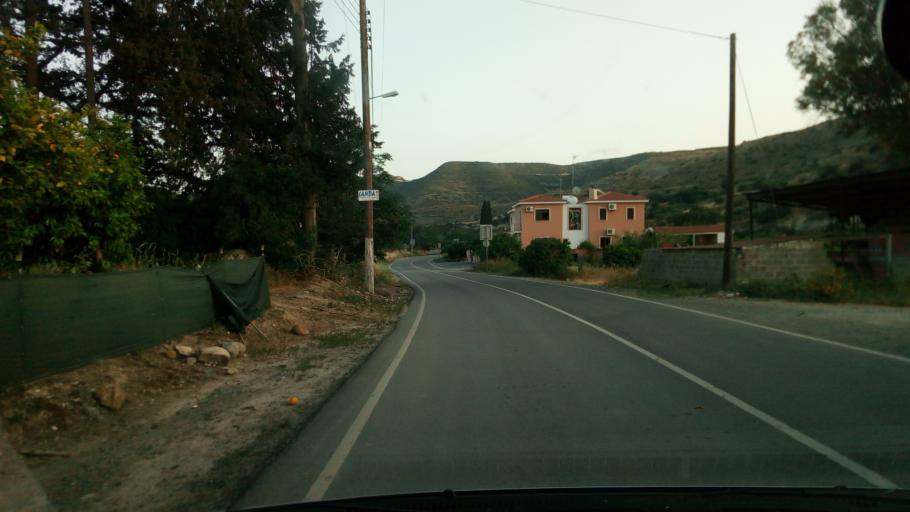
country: CY
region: Larnaka
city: Kofinou
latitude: 34.7940
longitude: 33.3847
